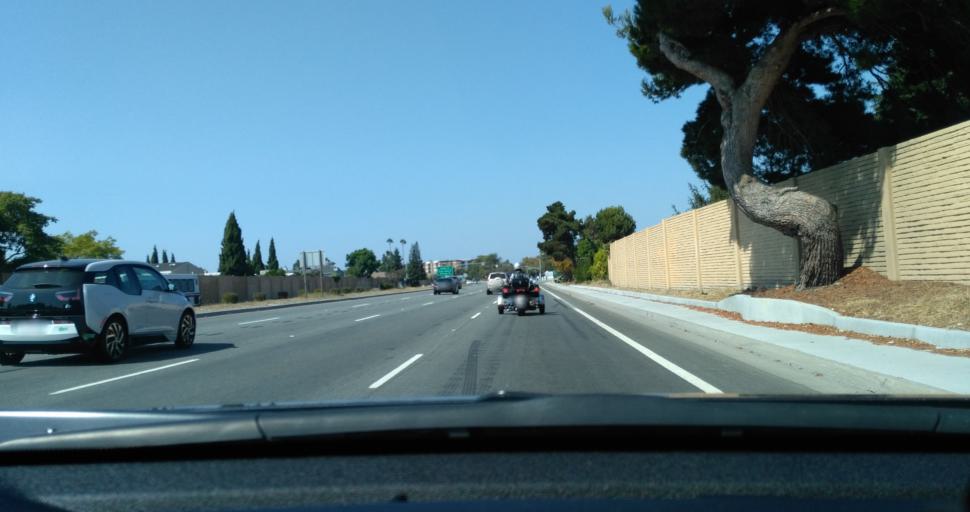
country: US
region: California
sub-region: Santa Clara County
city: Sunnyvale
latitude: 37.4005
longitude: -121.9956
